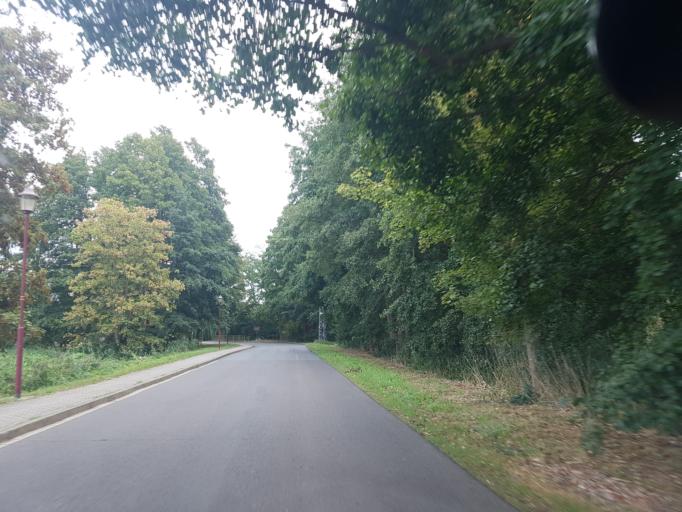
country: DE
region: Saxony-Anhalt
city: Klieken
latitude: 51.9554
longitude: 12.3060
